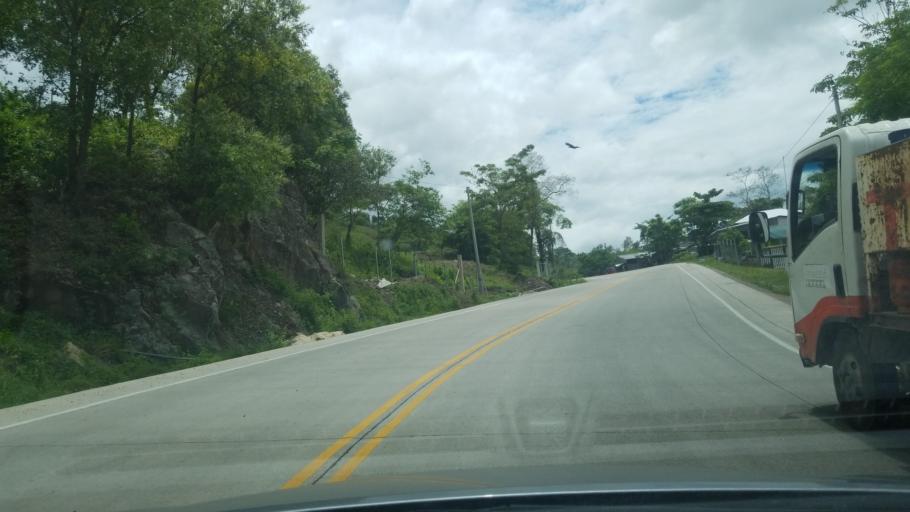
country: HN
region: Copan
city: San Jeronimo
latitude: 14.9821
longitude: -88.8508
